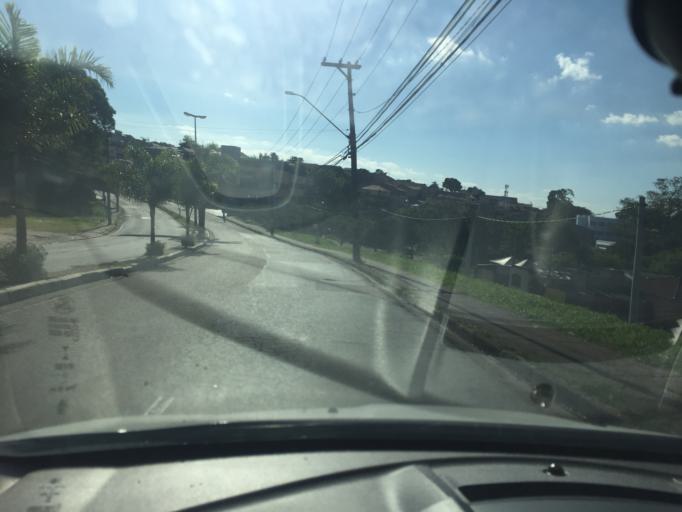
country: BR
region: Sao Paulo
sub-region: Varzea Paulista
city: Varzea Paulista
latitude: -23.2073
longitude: -46.8537
